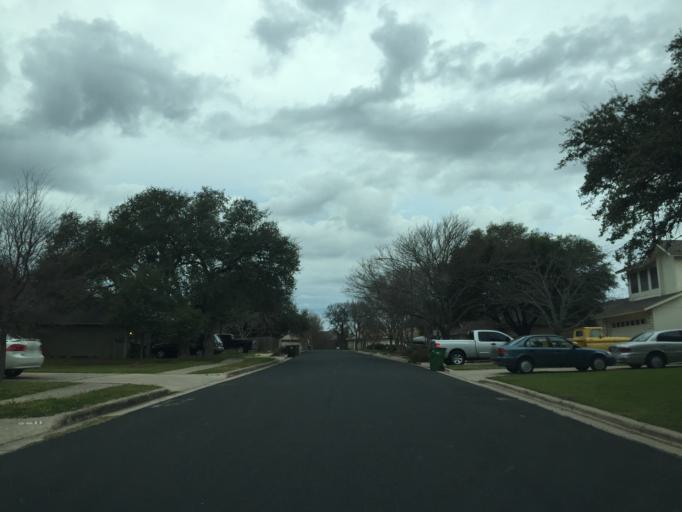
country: US
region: Texas
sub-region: Williamson County
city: Jollyville
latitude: 30.4481
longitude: -97.7461
